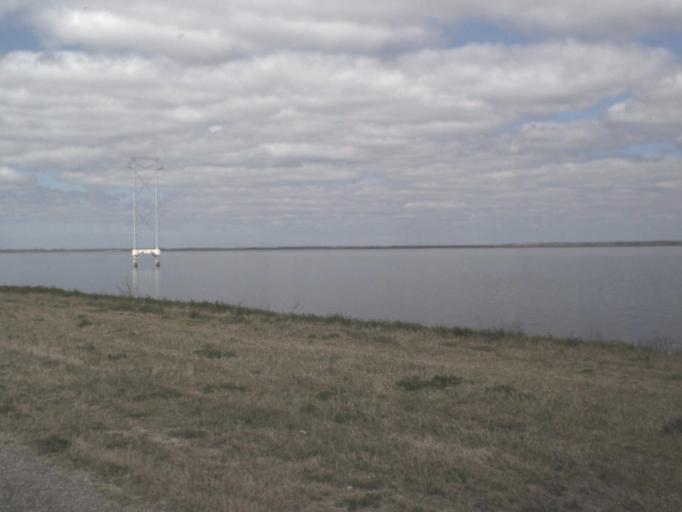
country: US
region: Florida
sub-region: Franklin County
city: Eastpoint
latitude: 29.7341
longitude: -84.9110
